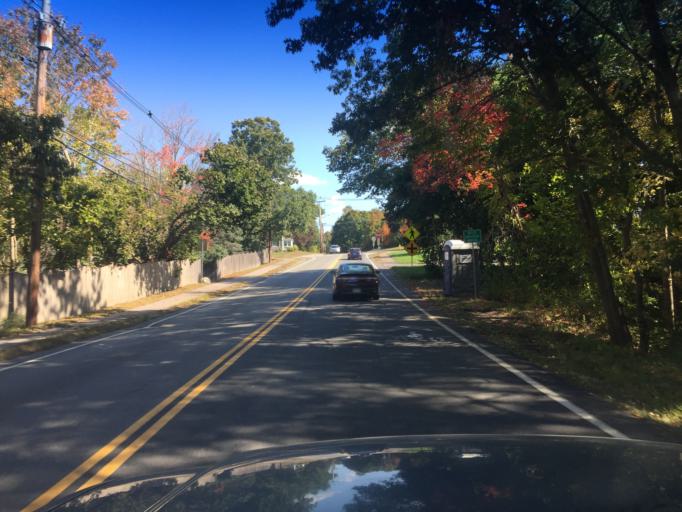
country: US
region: Massachusetts
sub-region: Norfolk County
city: Westwood
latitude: 42.2217
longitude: -71.2272
